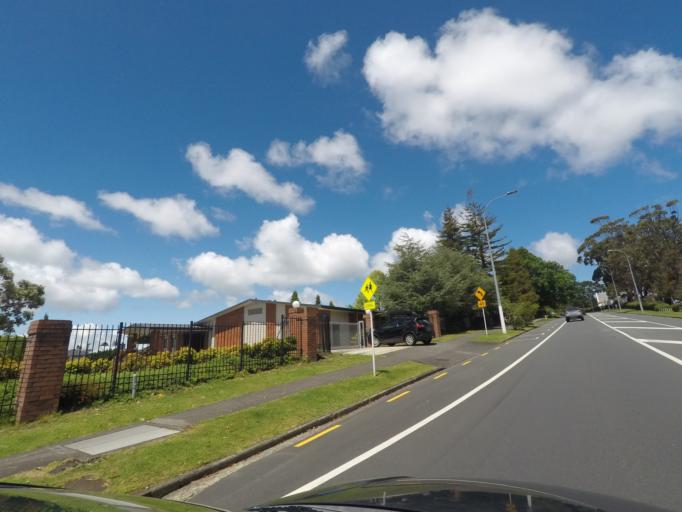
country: NZ
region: Auckland
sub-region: Auckland
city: Waitakere
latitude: -36.9066
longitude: 174.6524
